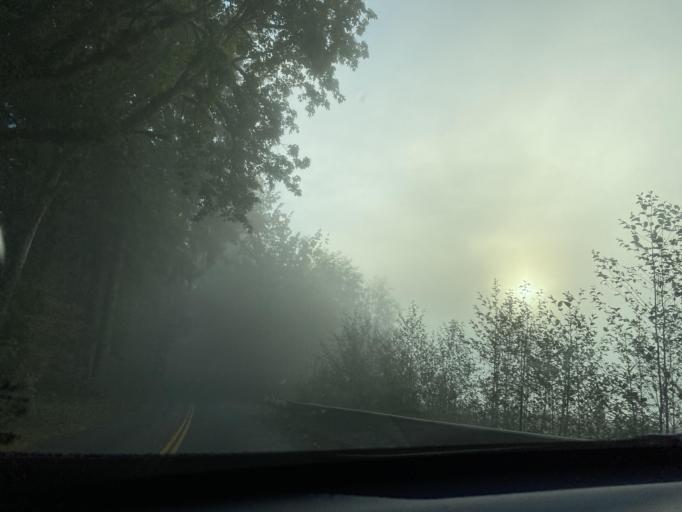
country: US
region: Washington
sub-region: Clallam County
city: Forks
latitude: 47.8104
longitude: -124.0794
